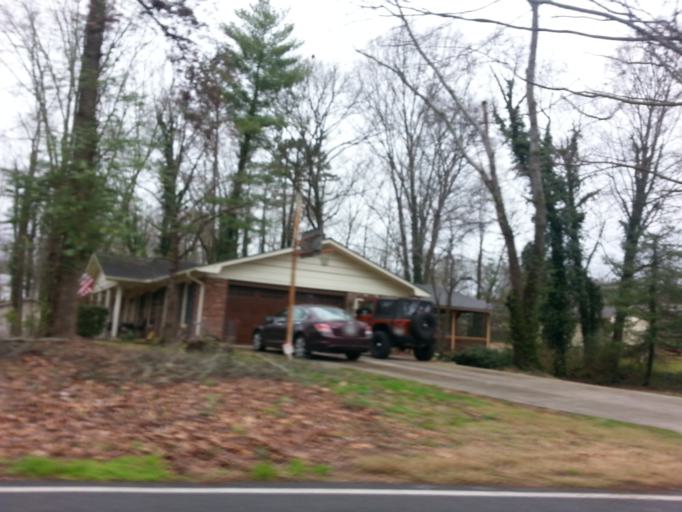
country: US
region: Tennessee
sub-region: Knox County
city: Knoxville
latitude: 35.9927
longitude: -84.0145
